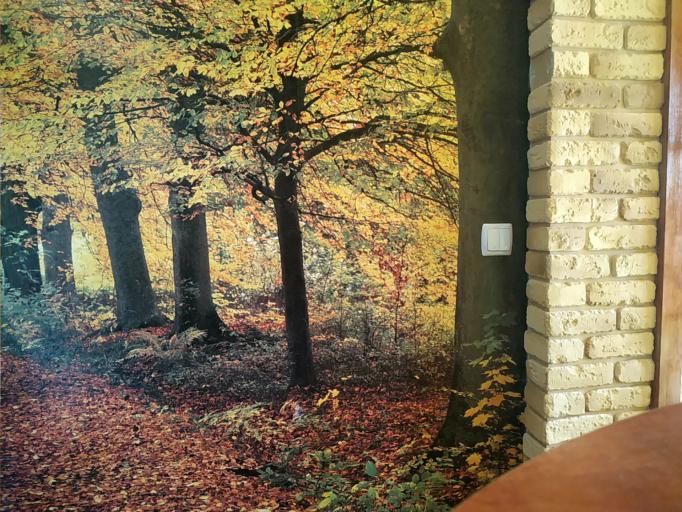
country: RU
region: Vologda
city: Molochnoye
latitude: 58.9712
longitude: 39.6313
